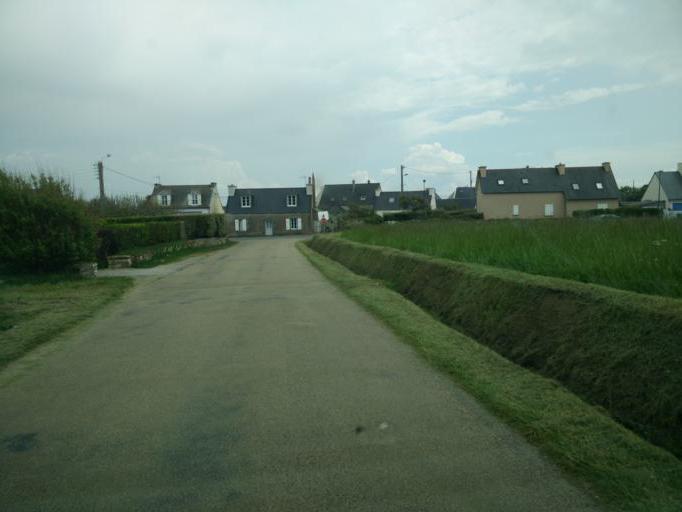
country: FR
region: Brittany
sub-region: Departement du Finistere
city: Camaret-sur-Mer
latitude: 48.2738
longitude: -4.6085
